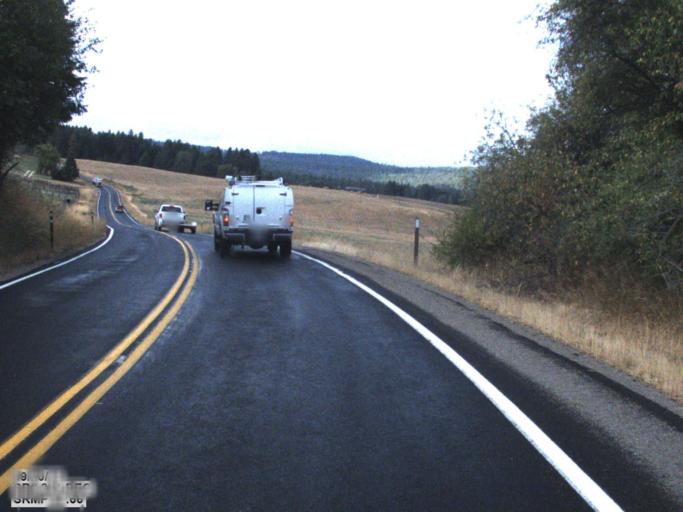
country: US
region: Washington
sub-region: Stevens County
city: Chewelah
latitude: 48.1225
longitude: -117.7501
